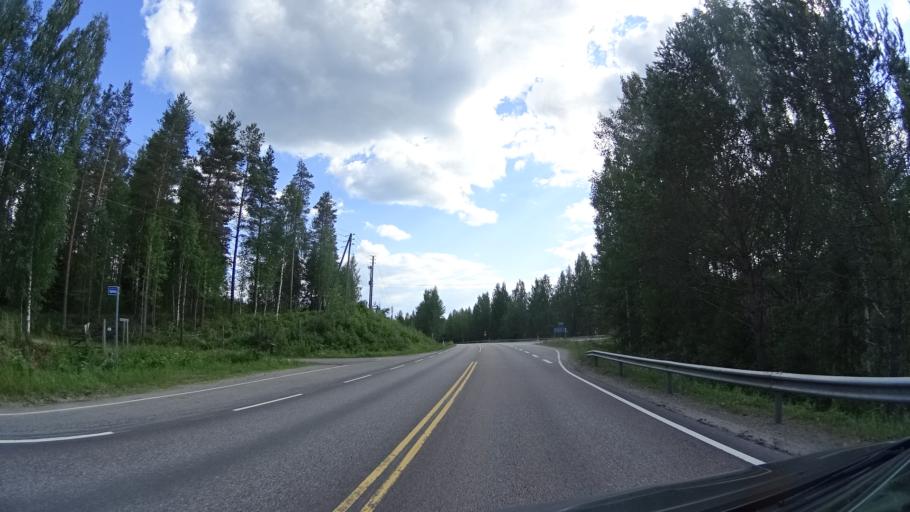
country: FI
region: Southern Savonia
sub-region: Savonlinna
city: Punkaharju
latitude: 61.6803
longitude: 29.4141
